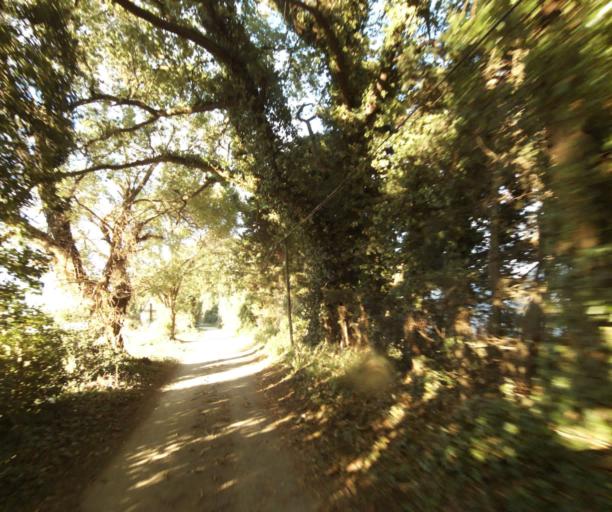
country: FR
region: Languedoc-Roussillon
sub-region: Departement des Pyrenees-Orientales
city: Argelers
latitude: 42.5755
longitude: 3.0122
